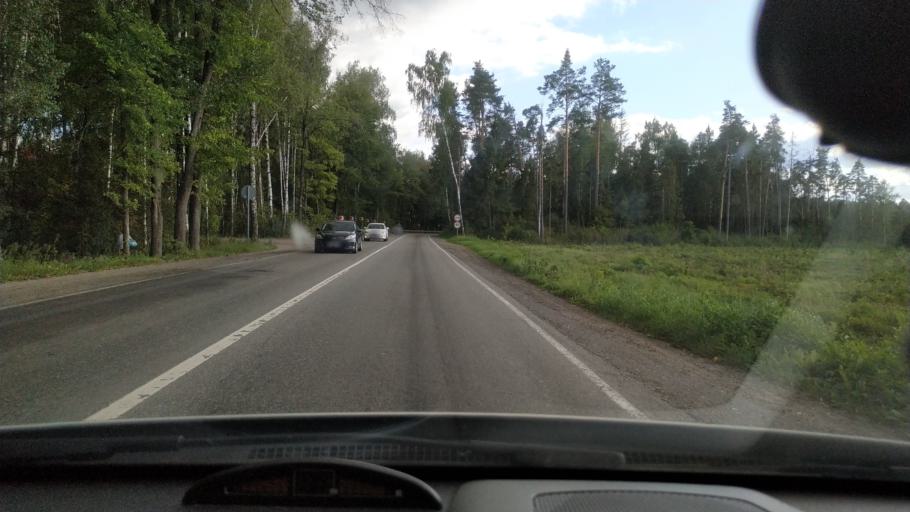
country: RU
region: Moskovskaya
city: Zheleznodorozhnyy
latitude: 55.7879
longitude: 38.0381
